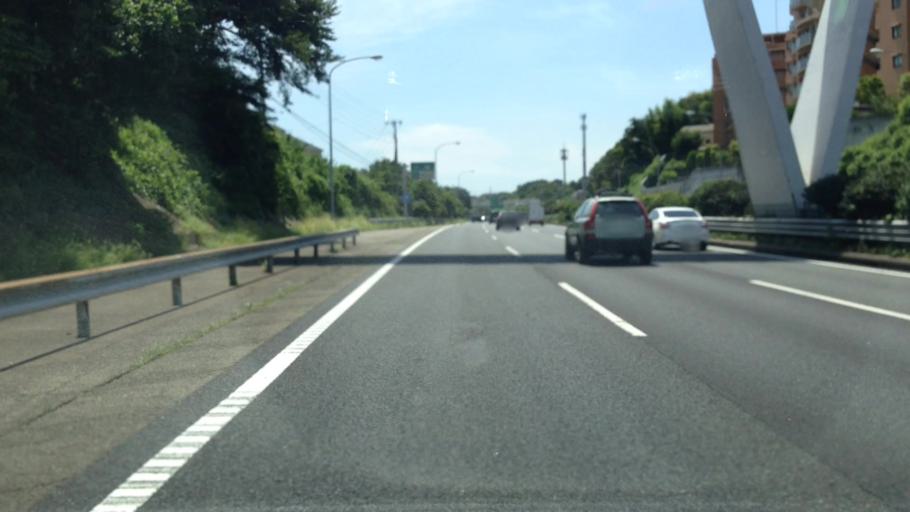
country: JP
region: Kanagawa
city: Yokohama
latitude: 35.5040
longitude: 139.5926
